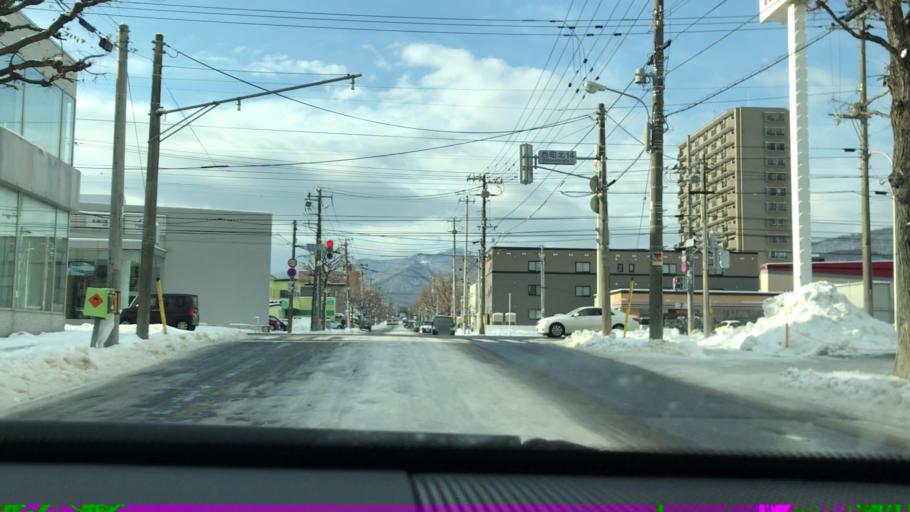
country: JP
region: Hokkaido
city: Sapporo
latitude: 43.0829
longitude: 141.2833
